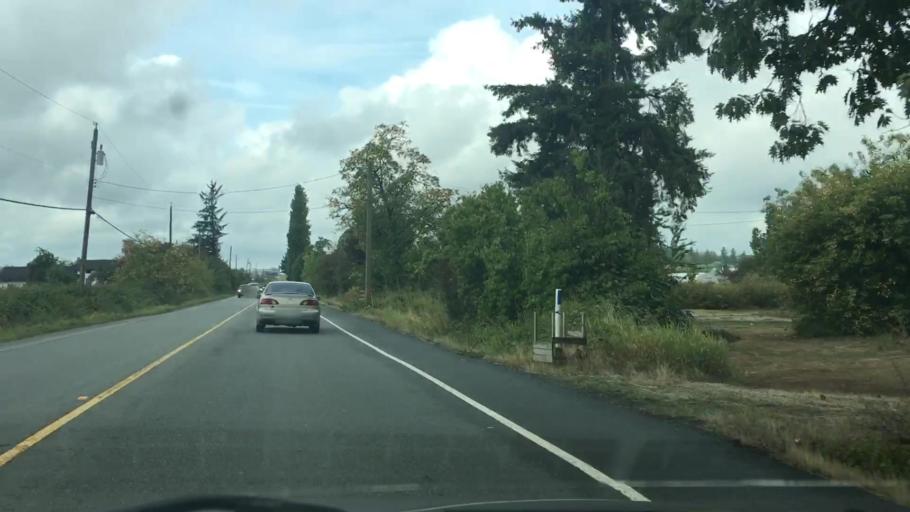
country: CA
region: British Columbia
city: Langley
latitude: 49.1043
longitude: -122.6097
